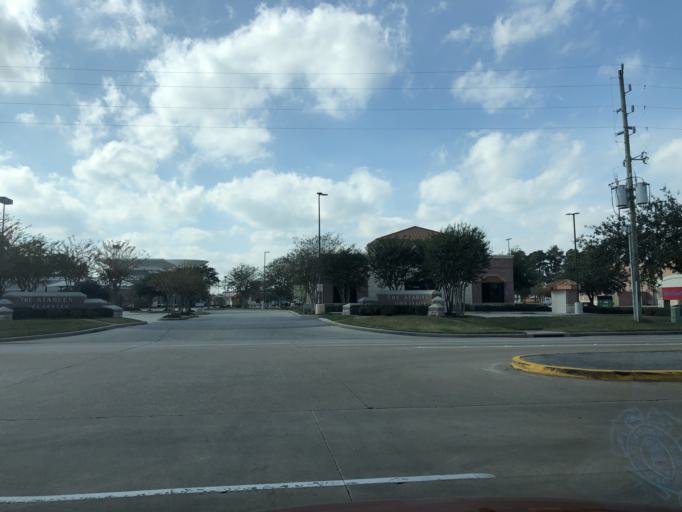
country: US
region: Texas
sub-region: Harris County
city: Tomball
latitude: 30.0320
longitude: -95.5540
